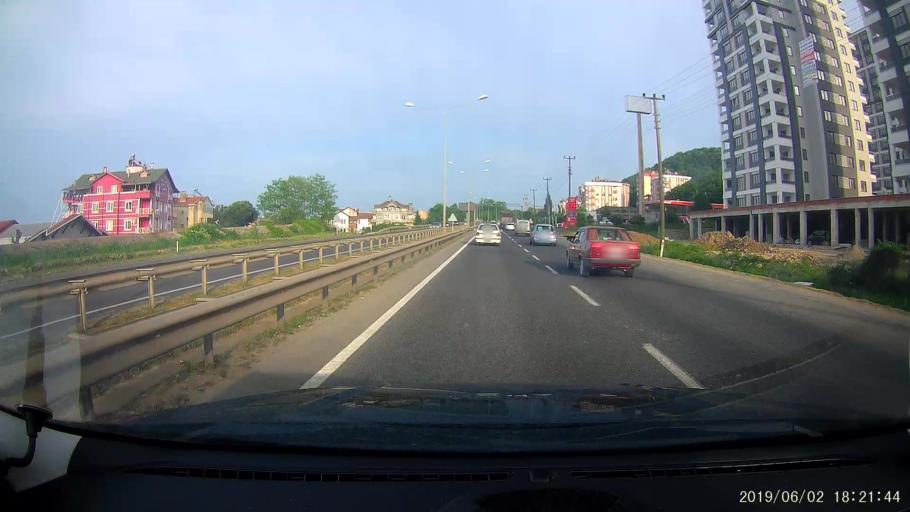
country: TR
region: Ordu
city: Fatsa
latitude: 41.0624
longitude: 37.4716
